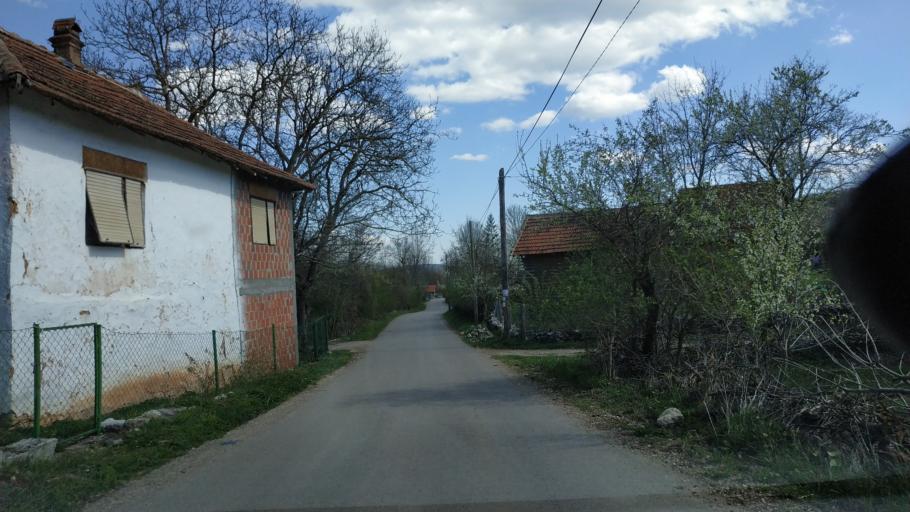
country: RS
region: Central Serbia
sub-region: Zajecarski Okrug
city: Soko Banja
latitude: 43.5727
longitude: 21.8991
